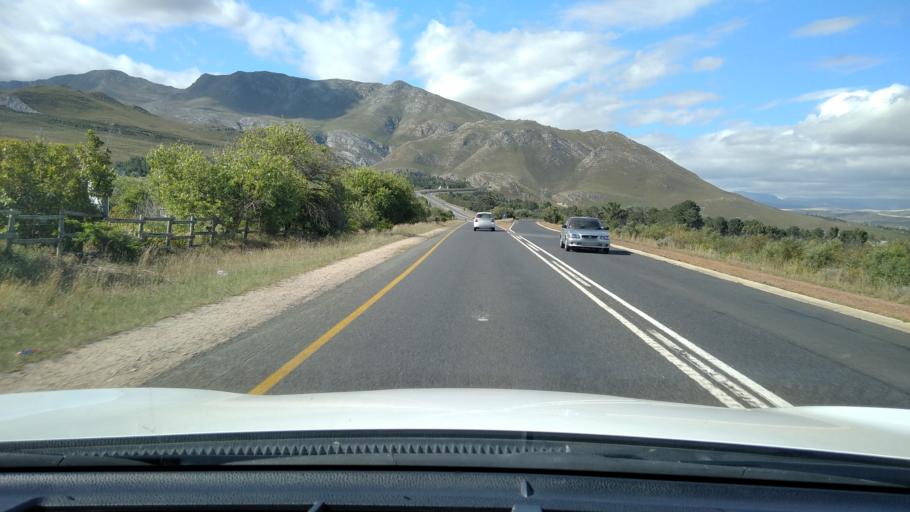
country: ZA
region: Western Cape
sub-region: Overberg District Municipality
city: Grabouw
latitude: -34.2332
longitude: 19.1865
